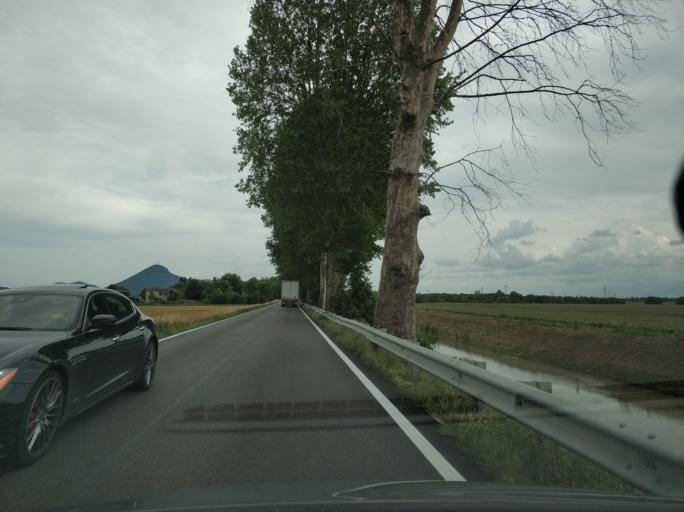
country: IT
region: Veneto
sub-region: Provincia di Padova
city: Lozzo Atestino
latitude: 45.2730
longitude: 11.5839
